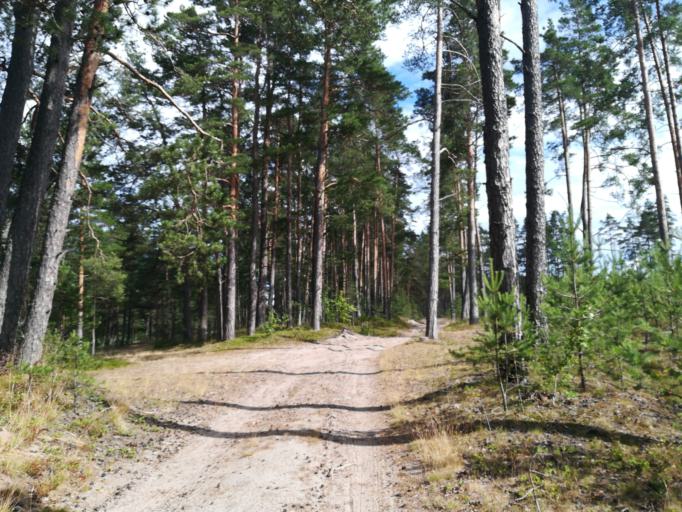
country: RU
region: Leningrad
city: Ust'-Luga
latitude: 59.6827
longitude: 28.2271
